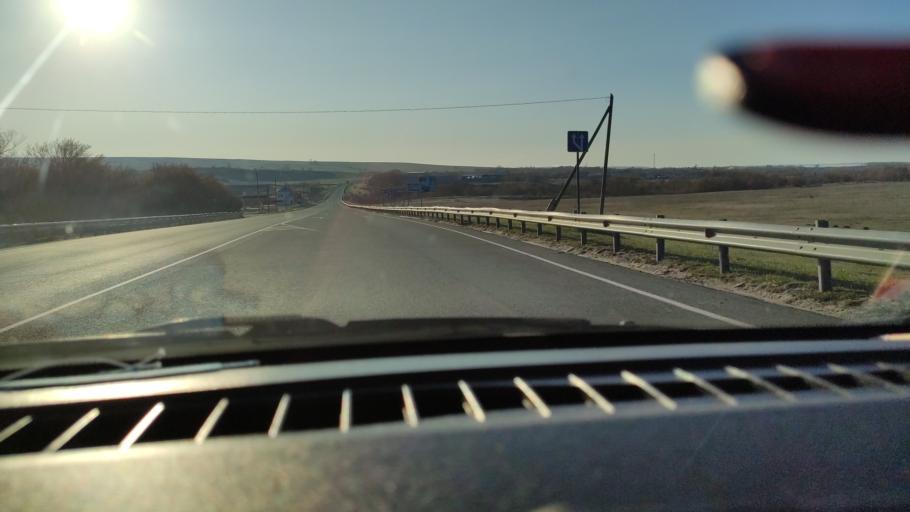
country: RU
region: Saratov
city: Tersa
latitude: 52.0986
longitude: 47.5233
